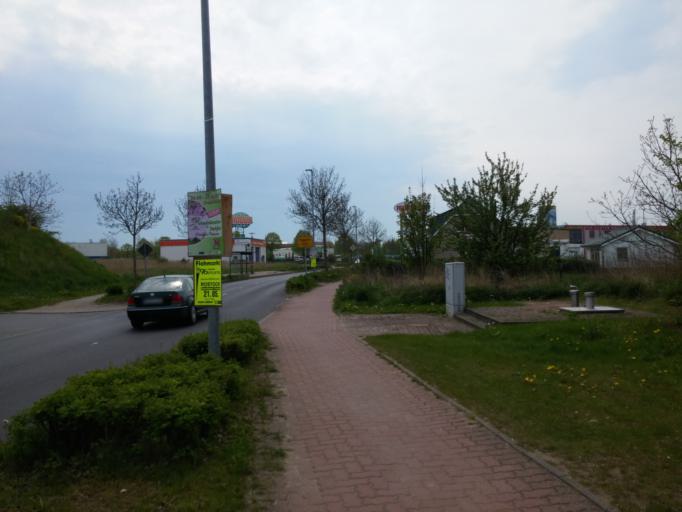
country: DE
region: Mecklenburg-Vorpommern
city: Roggentin
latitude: 54.0793
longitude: 12.1980
